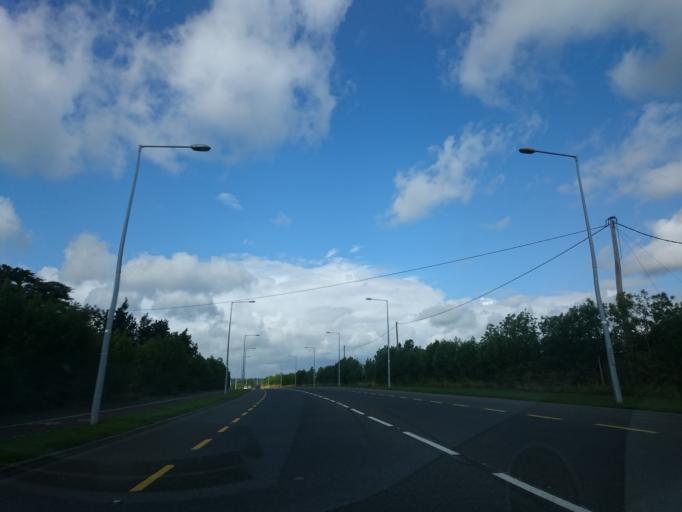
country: IE
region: Leinster
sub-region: Kilkenny
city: Kilkenny
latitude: 52.6753
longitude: -7.2378
